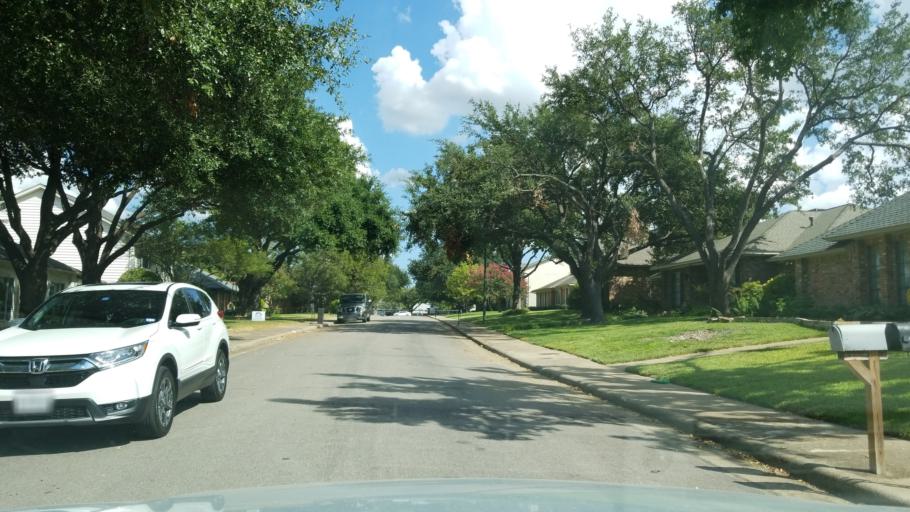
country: US
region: Texas
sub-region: Dallas County
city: Addison
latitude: 32.9613
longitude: -96.7938
